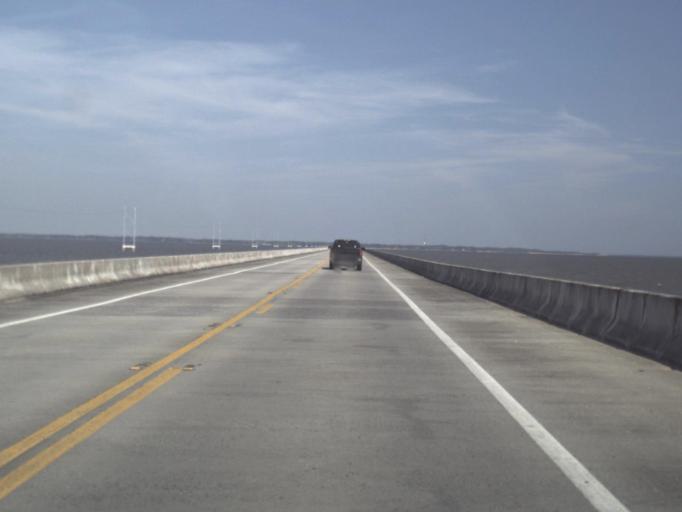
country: US
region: Florida
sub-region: Franklin County
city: Apalachicola
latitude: 29.7281
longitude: -84.9545
